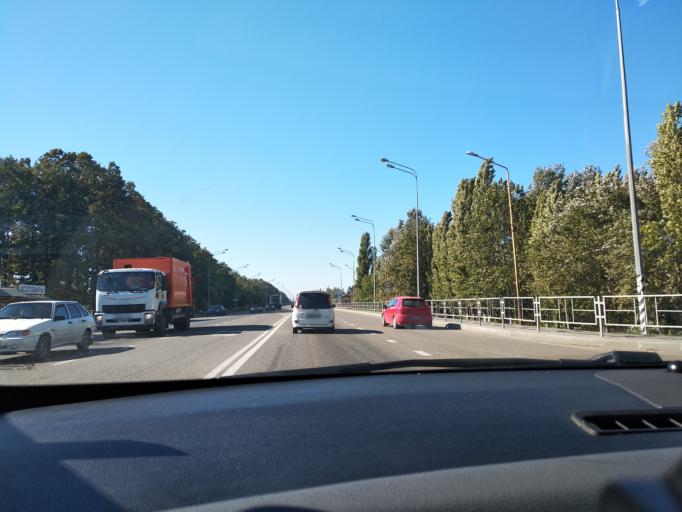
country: RU
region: Krasnodarskiy
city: Novotitarovskaya
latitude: 45.1502
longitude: 39.0584
